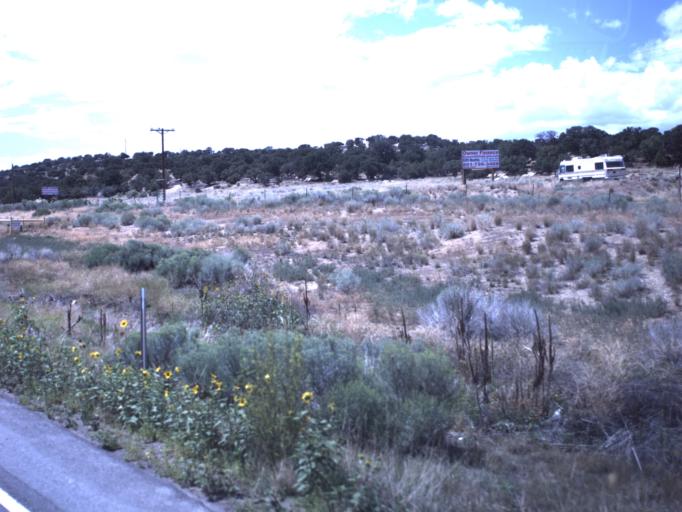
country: US
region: Utah
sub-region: Duchesne County
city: Duchesne
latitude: 40.1731
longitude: -110.5480
